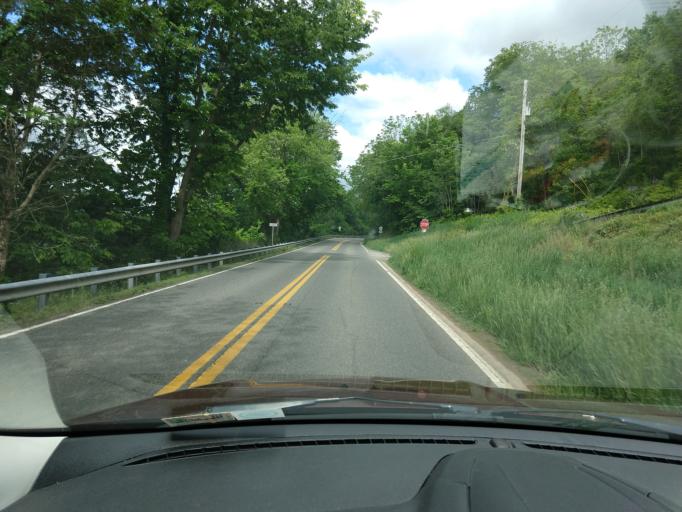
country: US
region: Virginia
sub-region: Wythe County
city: Wytheville
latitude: 36.8392
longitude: -80.9649
